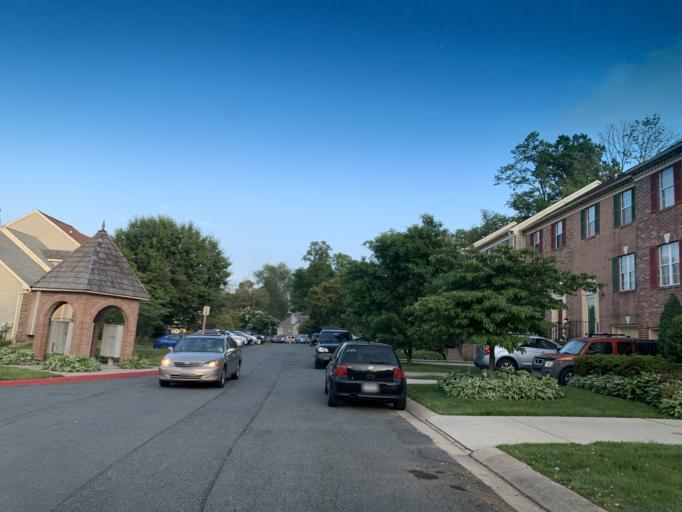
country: US
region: Maryland
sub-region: Harford County
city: North Bel Air
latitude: 39.5494
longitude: -76.3573
